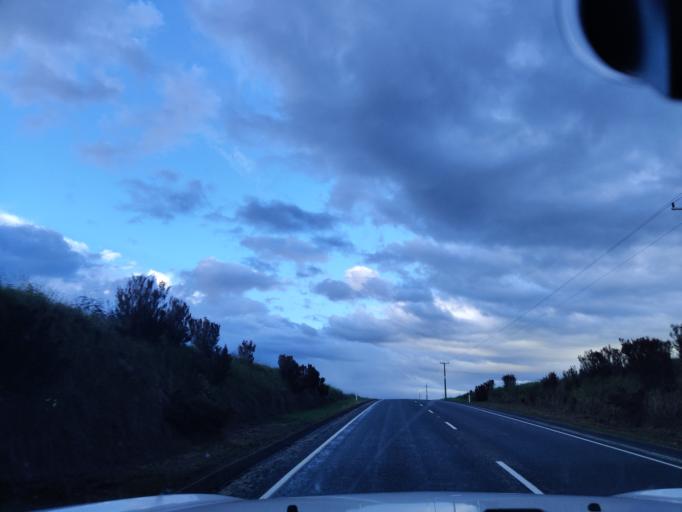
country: NZ
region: Waikato
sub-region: South Waikato District
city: Tokoroa
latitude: -38.3767
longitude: 175.7907
